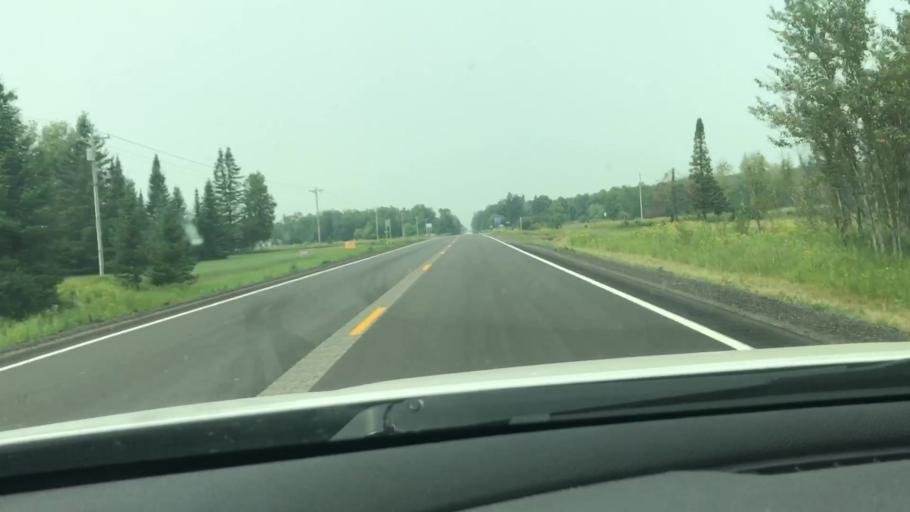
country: US
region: Minnesota
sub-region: Itasca County
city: Cohasset
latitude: 47.3543
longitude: -93.8474
